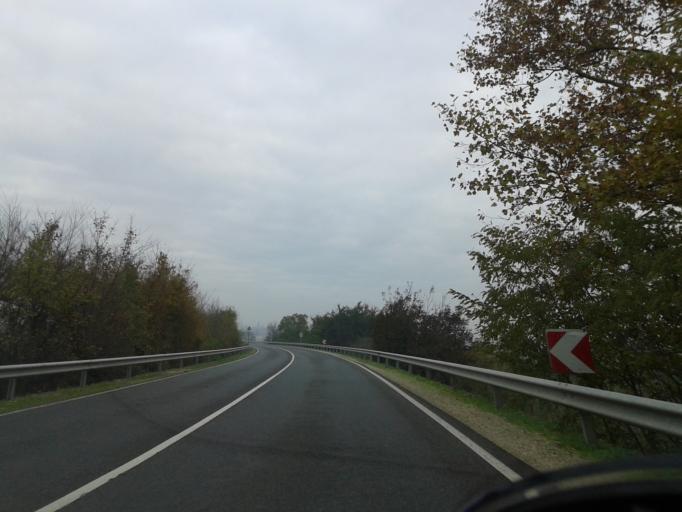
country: HU
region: Fejer
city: Ercsi
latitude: 47.2296
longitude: 18.8932
